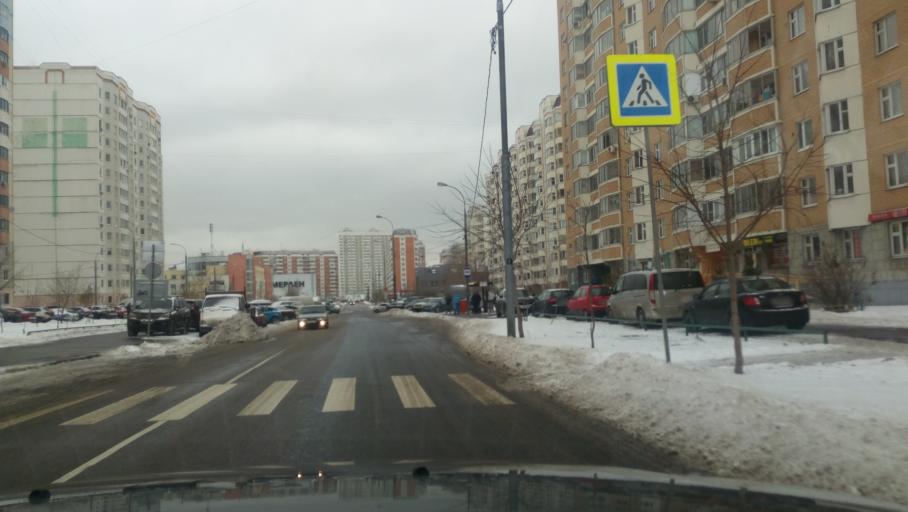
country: RU
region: Moscow
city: Nekrasovka
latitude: 55.7114
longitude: 37.8859
